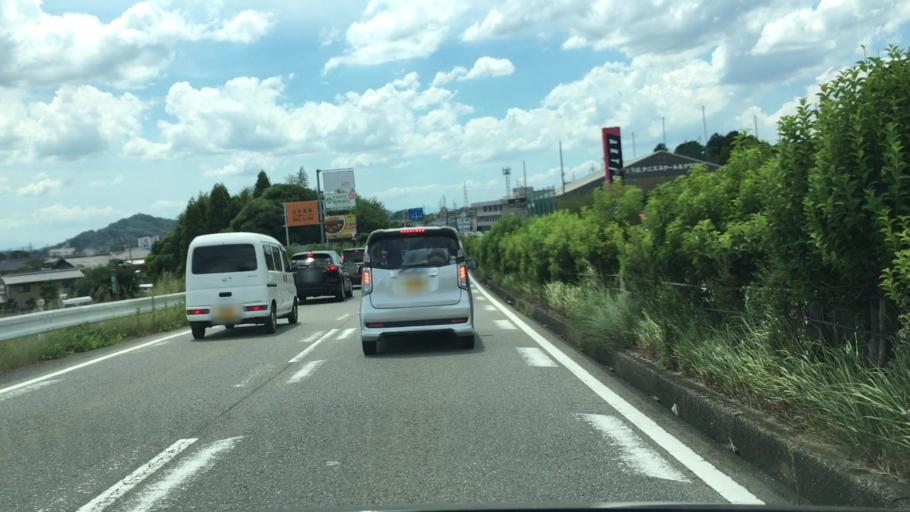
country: JP
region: Saga Prefecture
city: Tosu
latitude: 33.3921
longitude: 130.5024
